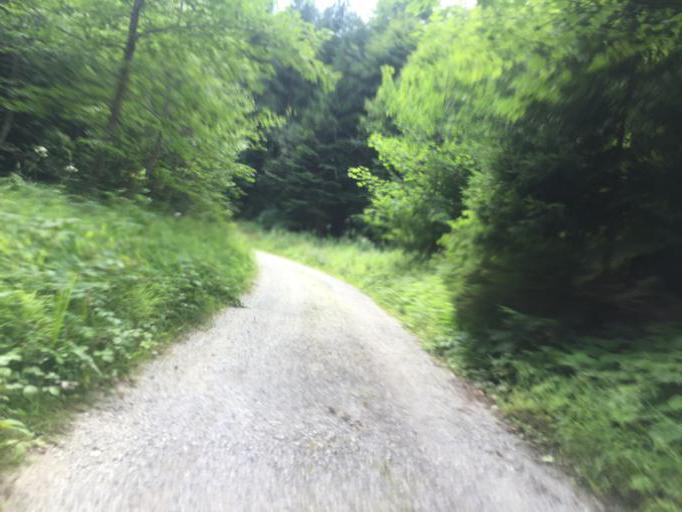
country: CH
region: Bern
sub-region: Thun District
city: Wattenwil
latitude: 46.7578
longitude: 7.4813
